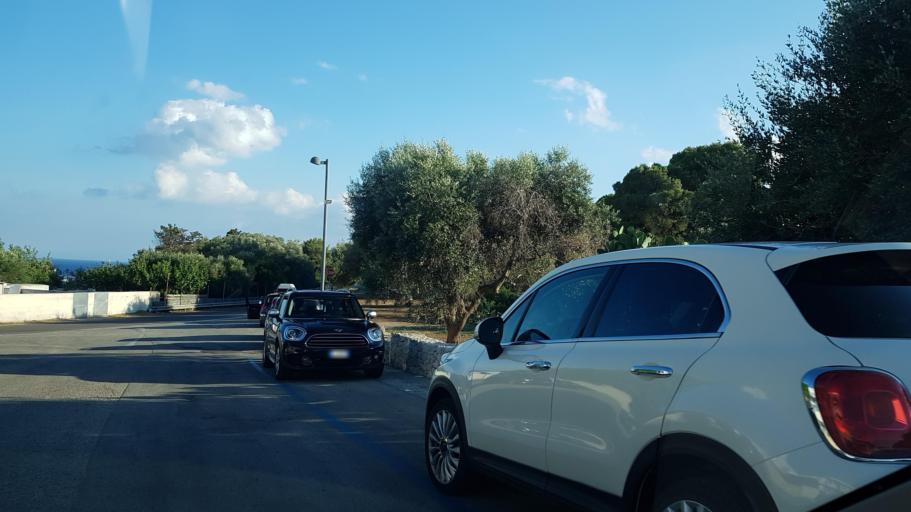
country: IT
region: Apulia
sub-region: Provincia di Lecce
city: Castro
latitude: 40.0028
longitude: 18.4215
